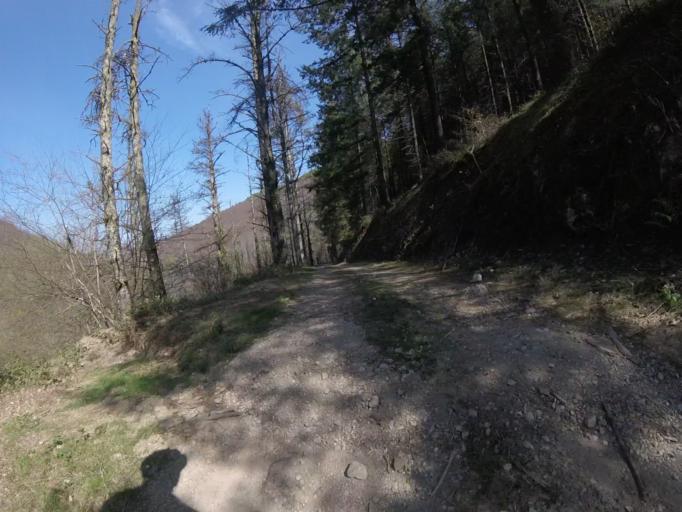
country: ES
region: Basque Country
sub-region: Provincia de Guipuzcoa
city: Irun
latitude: 43.2553
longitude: -1.8082
